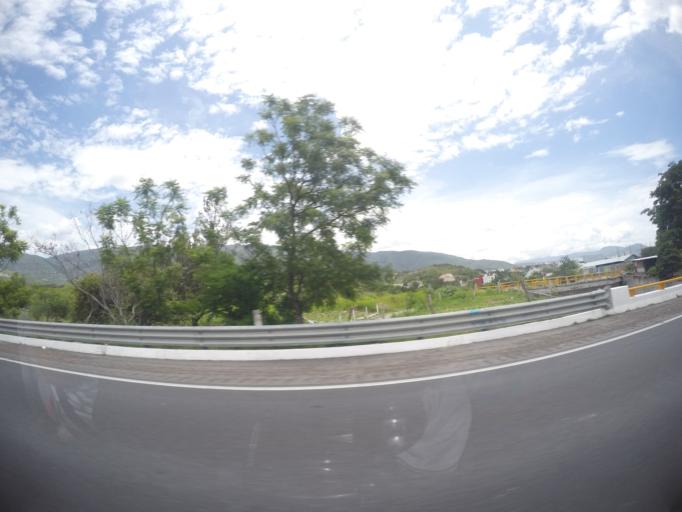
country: MX
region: Guerrero
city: Petaquillas
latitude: 17.5122
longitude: -99.4812
